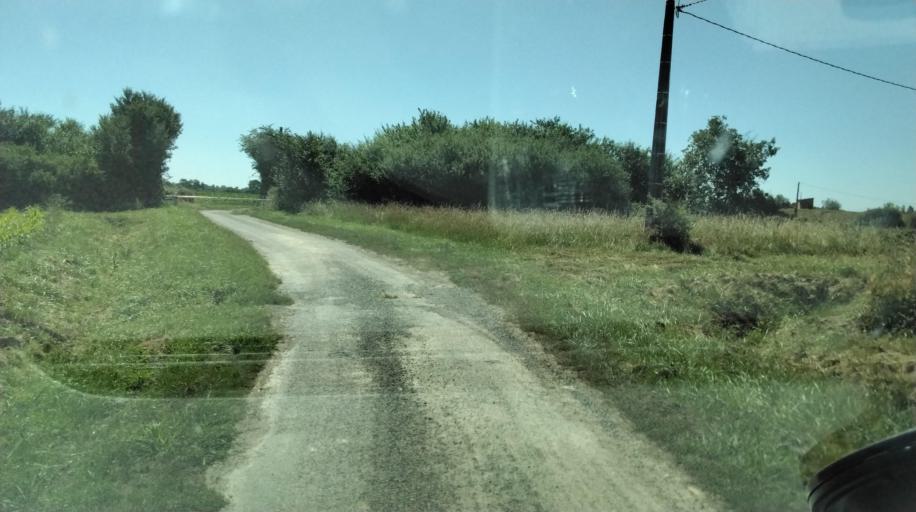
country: FR
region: Midi-Pyrenees
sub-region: Departement de la Haute-Garonne
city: Saint-Lys
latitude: 43.4991
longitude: 1.1644
